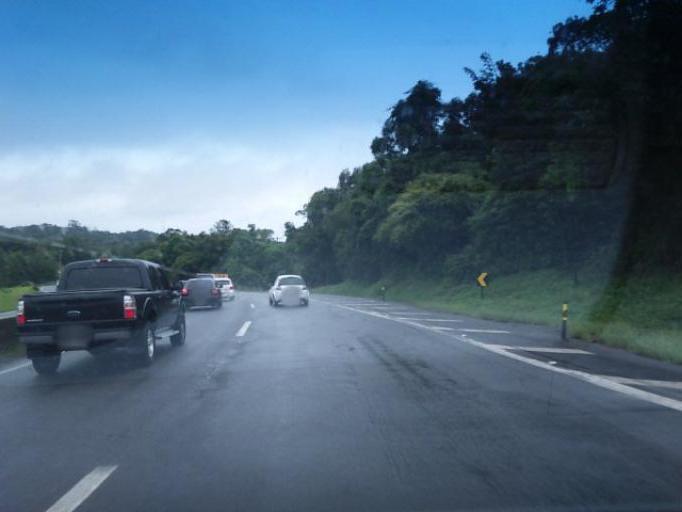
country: BR
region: Parana
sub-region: Sao Jose Dos Pinhais
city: Sao Jose dos Pinhais
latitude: -25.8410
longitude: -49.0478
